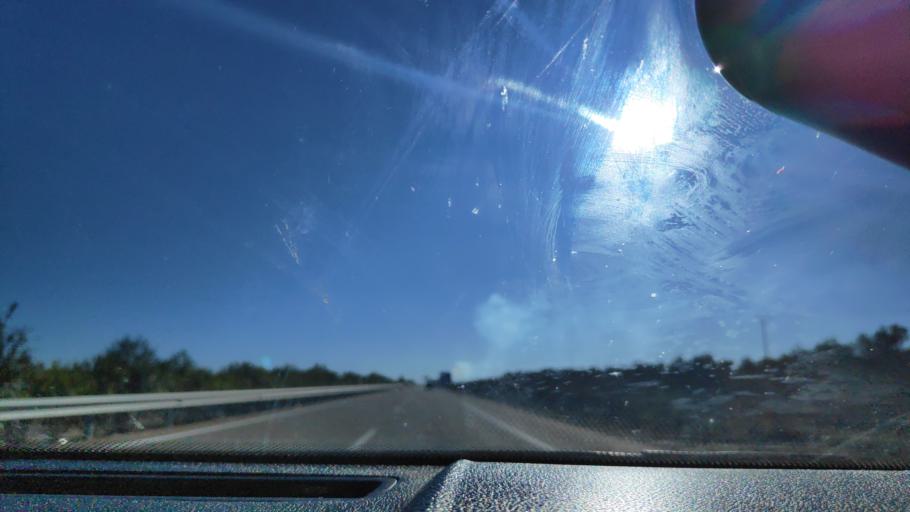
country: ES
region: Extremadura
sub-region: Provincia de Badajoz
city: Los Santos de Maimona
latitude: 38.4840
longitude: -6.3571
